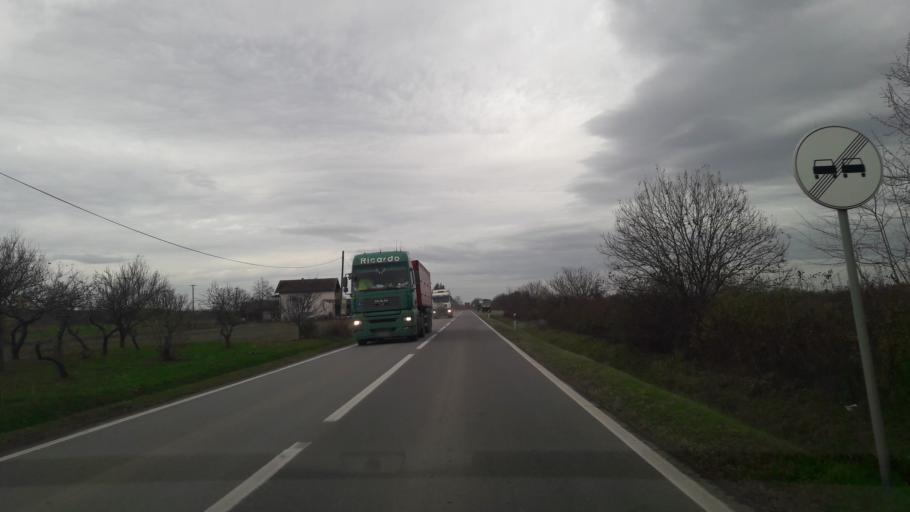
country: HR
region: Osjecko-Baranjska
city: Fericanci
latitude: 45.5326
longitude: 17.9446
